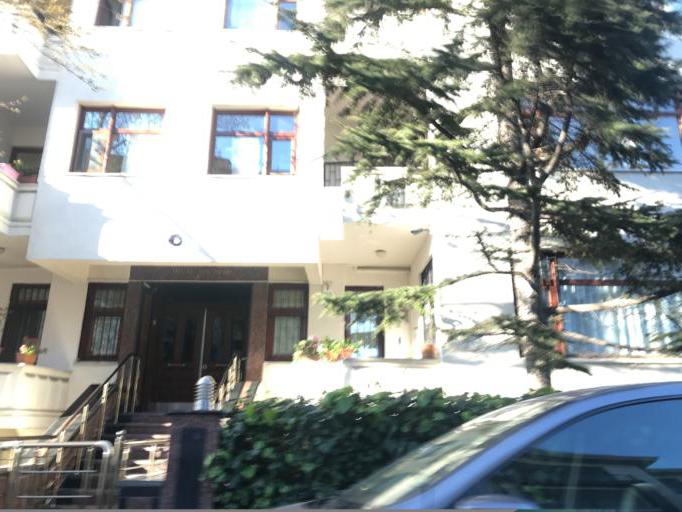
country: TR
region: Istanbul
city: Bahcelievler
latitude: 40.9599
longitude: 28.8295
